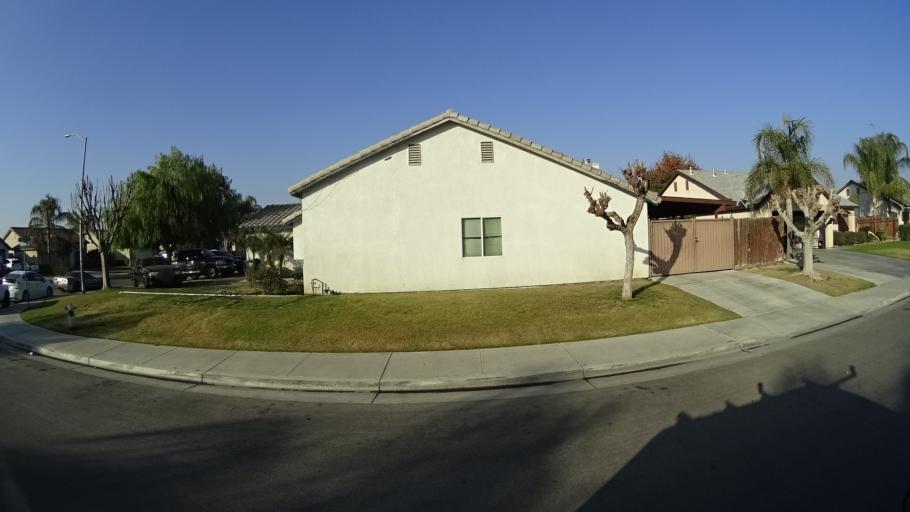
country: US
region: California
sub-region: Kern County
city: Greenfield
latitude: 35.2853
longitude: -119.0091
